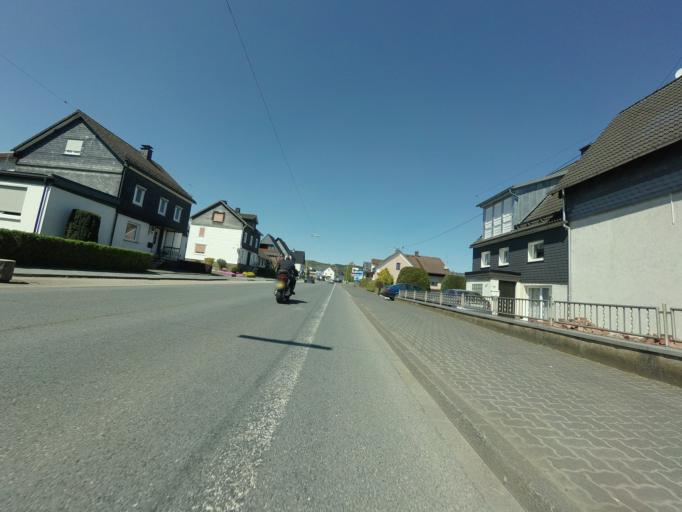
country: DE
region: North Rhine-Westphalia
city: Kreuztal
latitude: 50.9810
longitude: 7.9663
